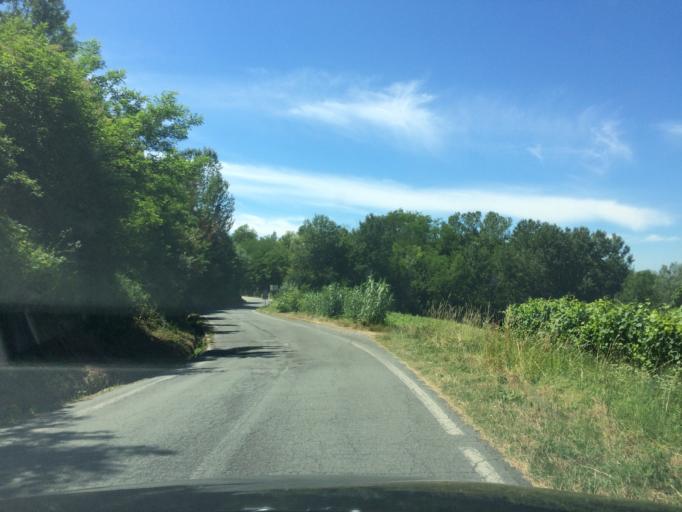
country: IT
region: Piedmont
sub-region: Provincia di Asti
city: Castel Rocchero
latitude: 44.7109
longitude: 8.4354
